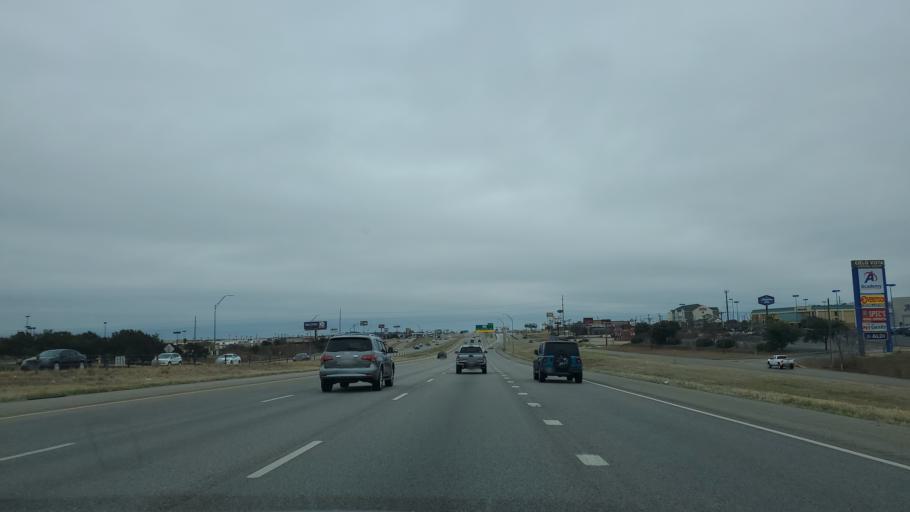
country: US
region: Texas
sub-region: Bell County
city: Killeen
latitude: 31.0901
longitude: -97.7186
